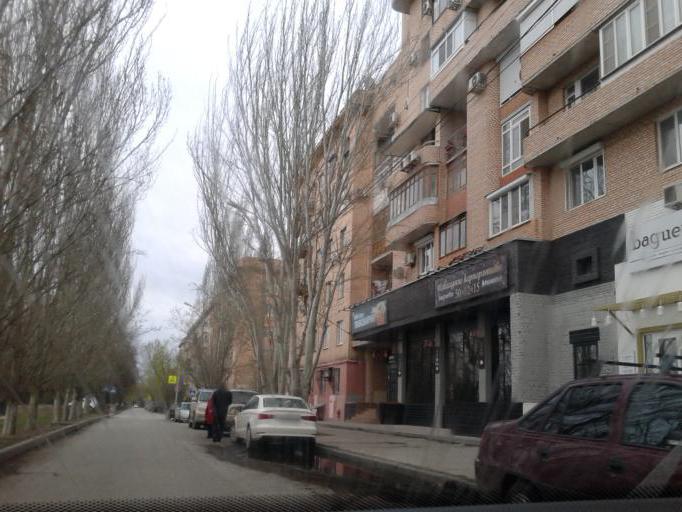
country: RU
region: Volgograd
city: Volgograd
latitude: 48.7116
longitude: 44.5305
